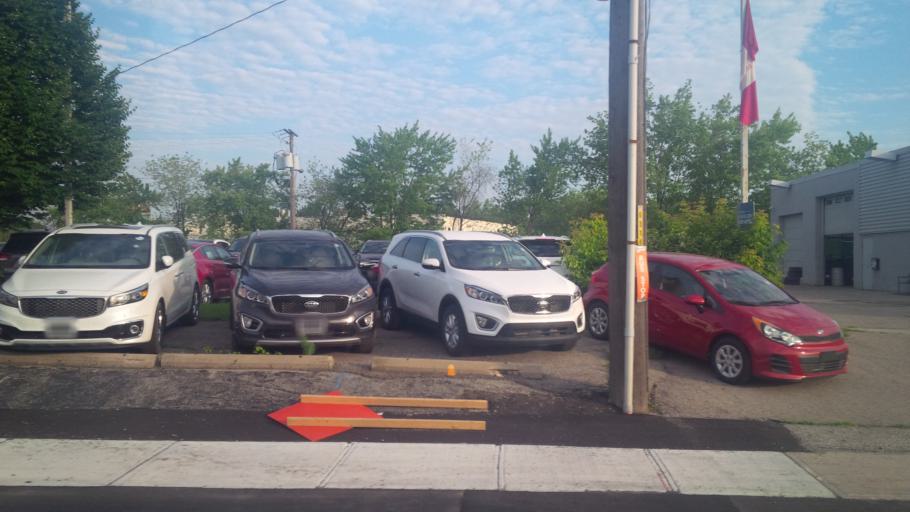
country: CA
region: Ontario
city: Etobicoke
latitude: 43.7101
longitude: -79.6358
